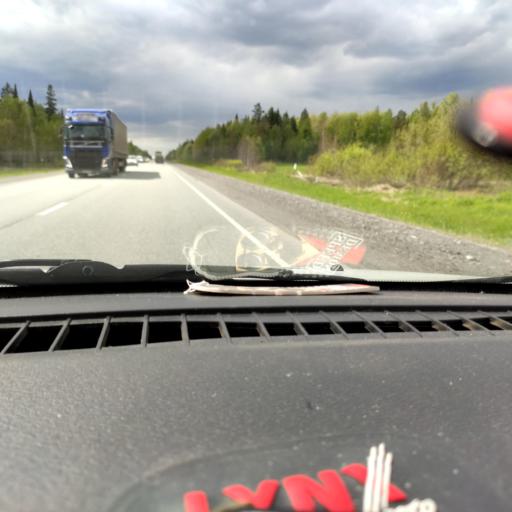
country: RU
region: Sverdlovsk
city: Druzhinino
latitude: 56.7972
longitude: 59.4463
